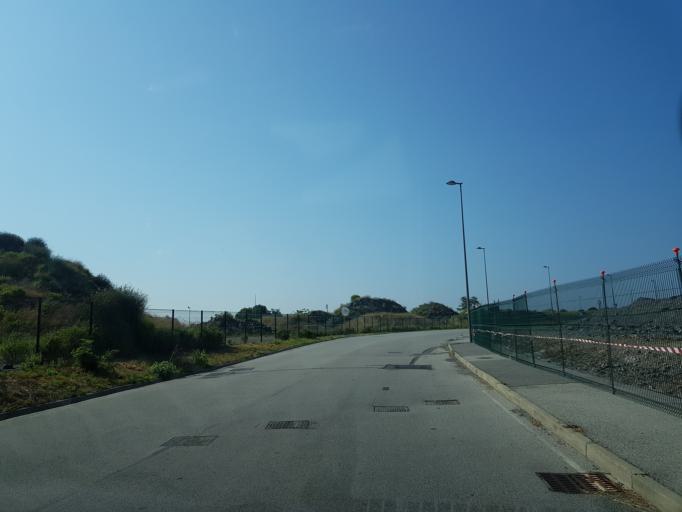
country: IT
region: Liguria
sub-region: Provincia di Genova
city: San Teodoro
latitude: 44.4249
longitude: 8.8645
